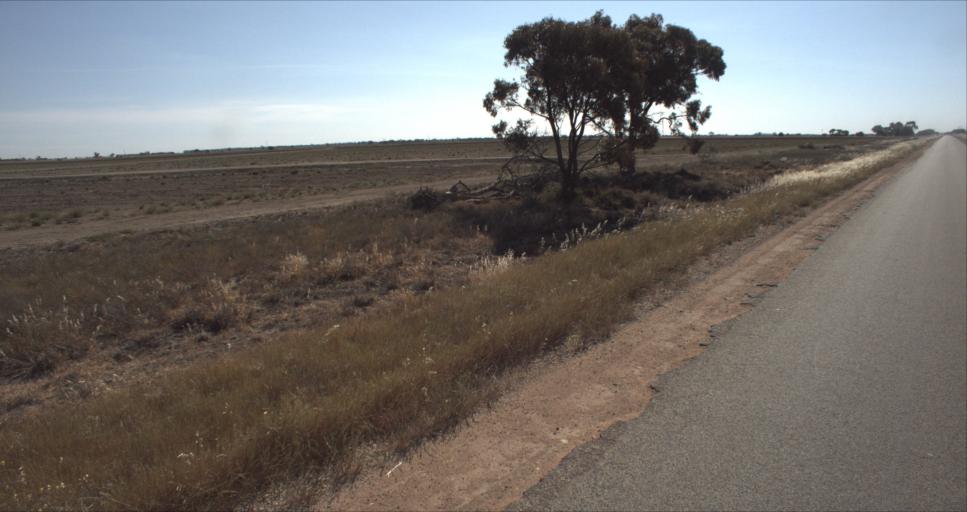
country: AU
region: New South Wales
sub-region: Leeton
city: Leeton
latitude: -34.4835
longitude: 146.3742
